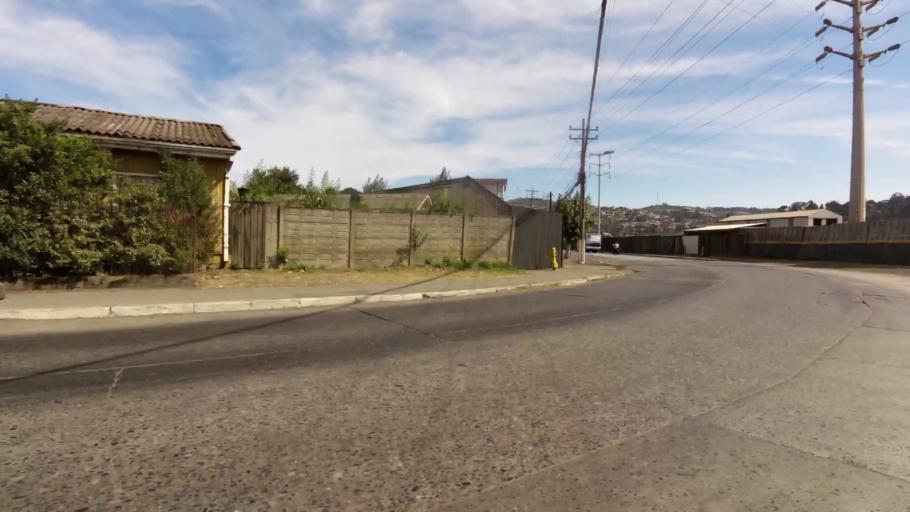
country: CL
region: Biobio
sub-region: Provincia de Concepcion
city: Talcahuano
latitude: -36.7266
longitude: -73.1166
